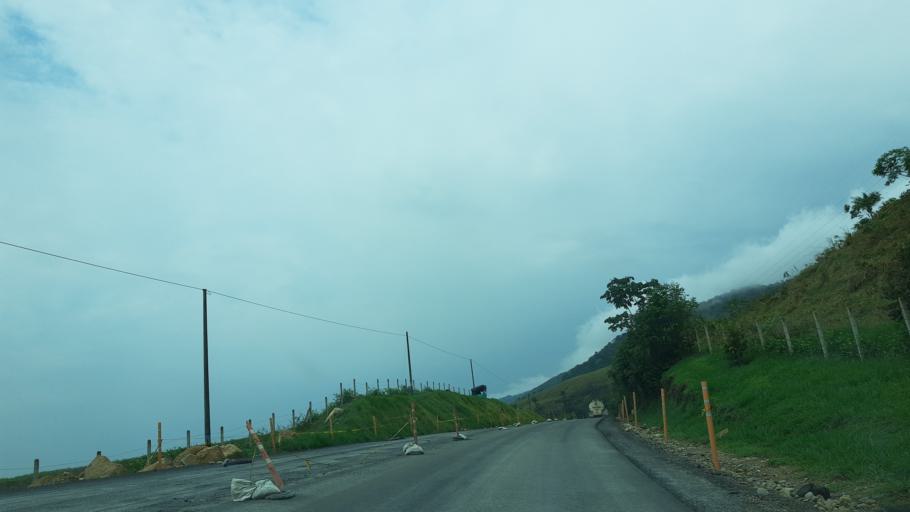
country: CO
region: Casanare
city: Sabanalarga
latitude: 4.8107
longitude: -72.9769
